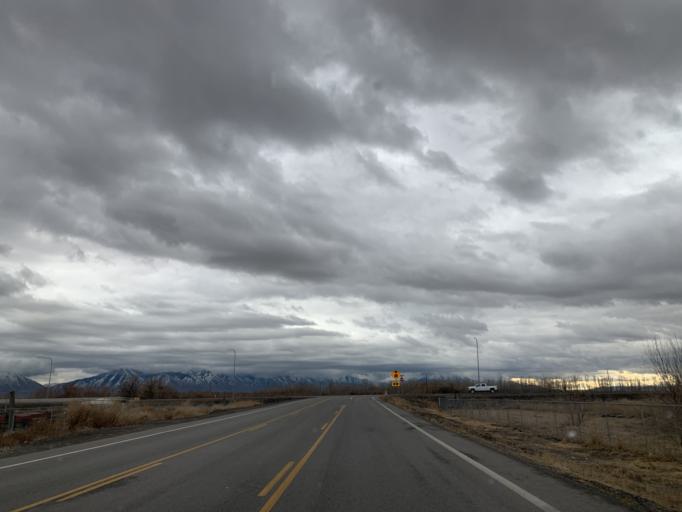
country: US
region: Utah
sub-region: Utah County
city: Provo
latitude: 40.2115
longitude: -111.6777
